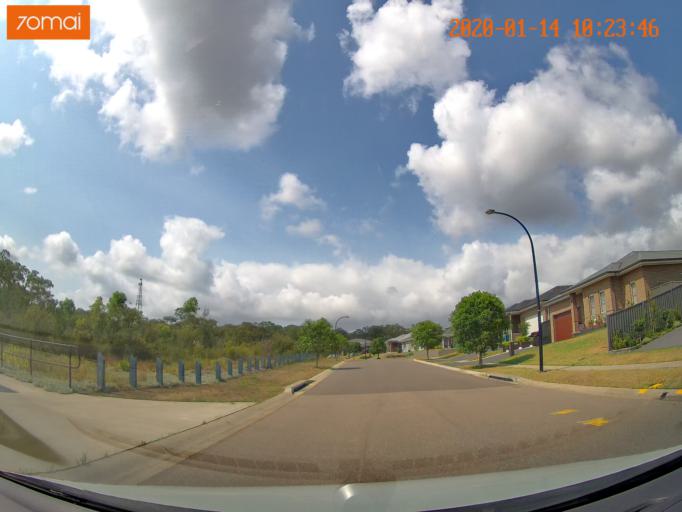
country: AU
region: New South Wales
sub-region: Lake Macquarie Shire
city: Dora Creek
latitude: -33.1093
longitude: 151.5115
